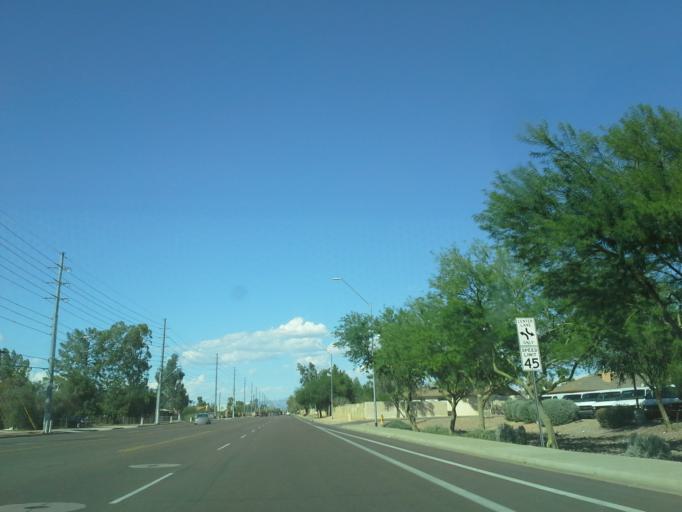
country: US
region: Arizona
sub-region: Maricopa County
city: Paradise Valley
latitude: 33.6415
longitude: -112.0134
